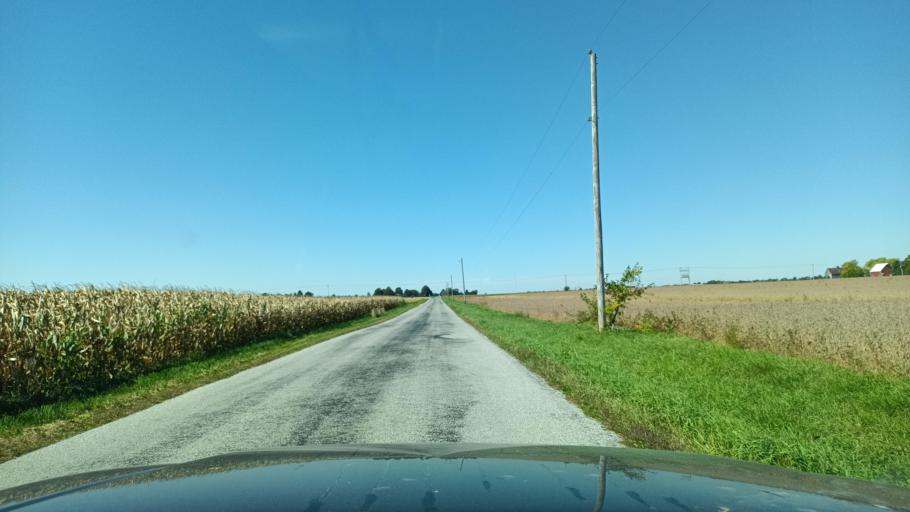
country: US
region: Illinois
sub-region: Champaign County
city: Mahomet
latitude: 40.0988
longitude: -88.3648
